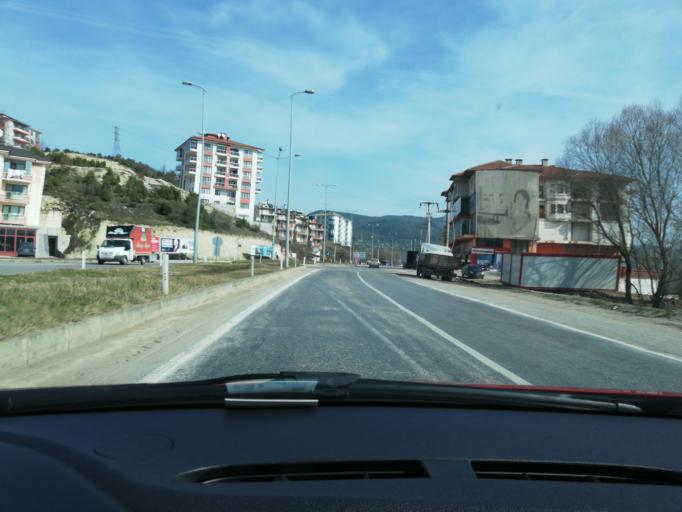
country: TR
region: Bartin
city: Bartin
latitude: 41.6423
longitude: 32.3561
